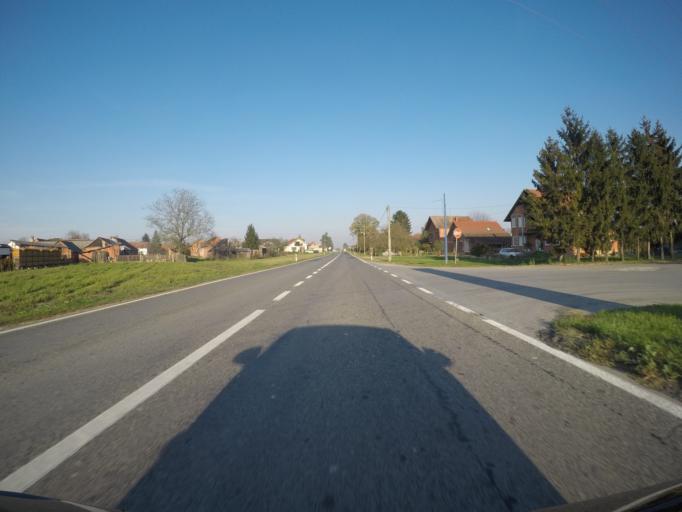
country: HR
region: Virovitick-Podravska
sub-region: Grad Virovitica
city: Virovitica
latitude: 45.8854
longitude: 17.4111
